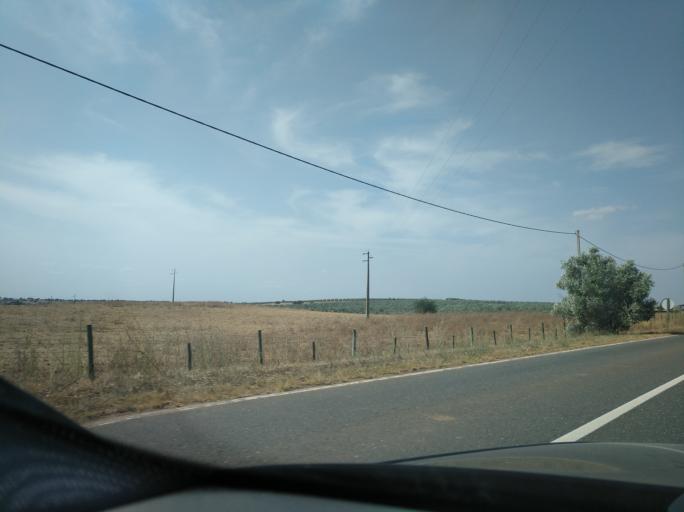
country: PT
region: Beja
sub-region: Beja
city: Beja
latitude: 37.8592
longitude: -7.8618
